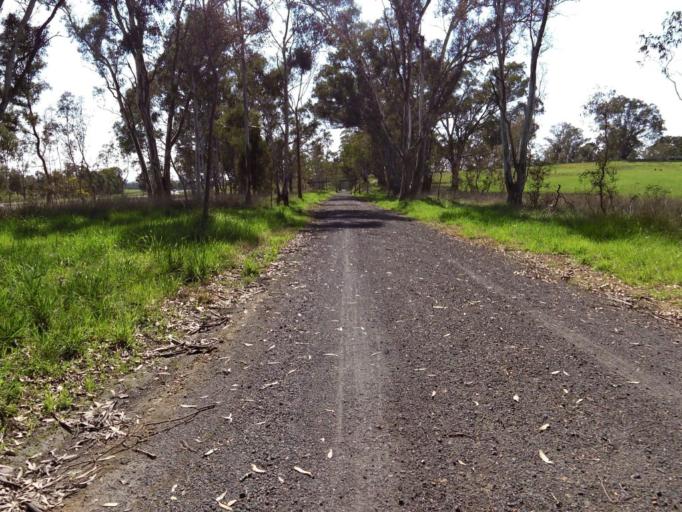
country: AU
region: Victoria
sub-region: Murrindindi
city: Alexandra
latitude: -37.1183
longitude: 145.6043
